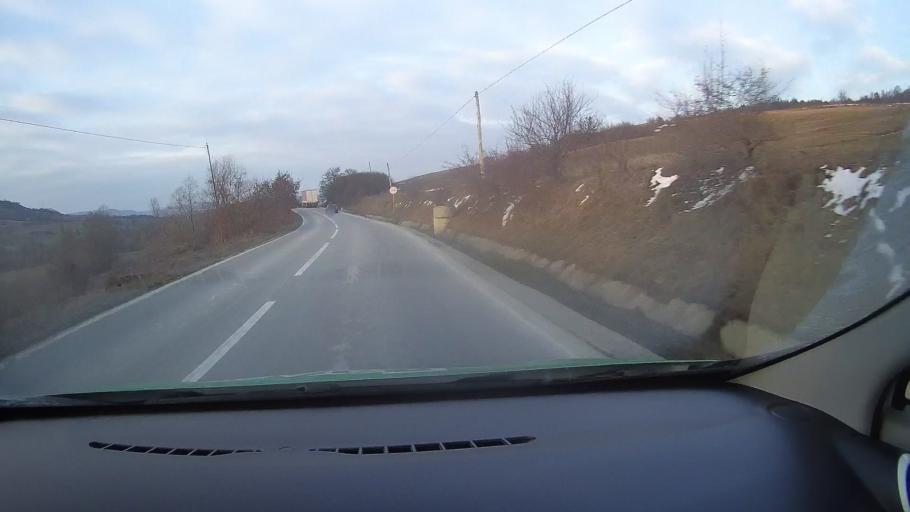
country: RO
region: Harghita
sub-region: Comuna Simonesti
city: Simonesti
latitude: 46.3247
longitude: 25.1016
